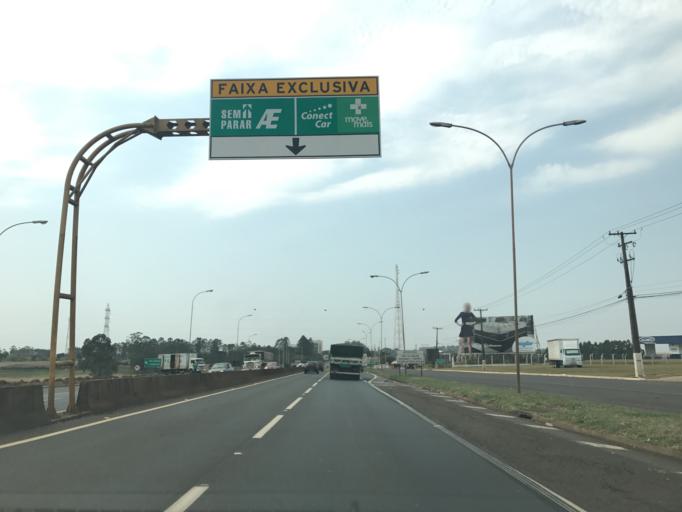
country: BR
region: Parana
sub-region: Arapongas
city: Arapongas
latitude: -23.3640
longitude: -51.4025
